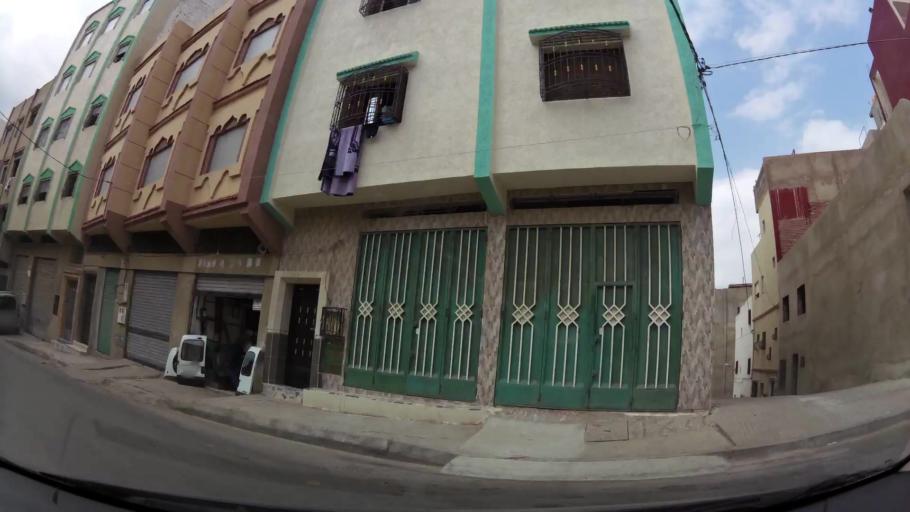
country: MA
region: Tanger-Tetouan
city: Tetouan
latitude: 35.5678
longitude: -5.3953
